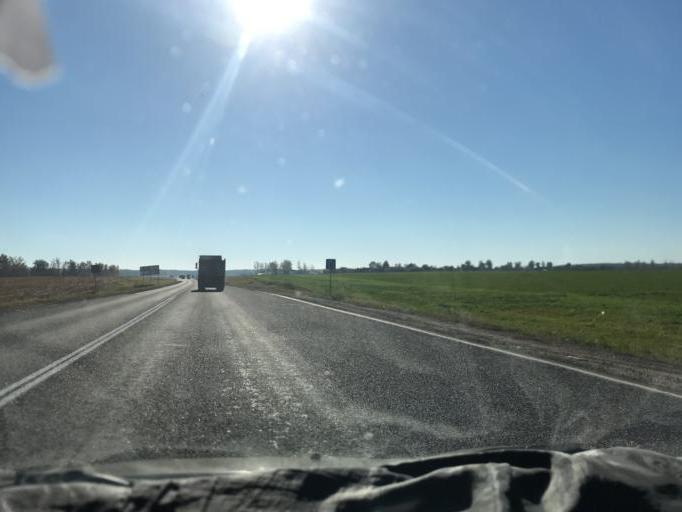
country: BY
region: Mogilev
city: Babruysk
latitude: 53.0762
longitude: 29.0707
